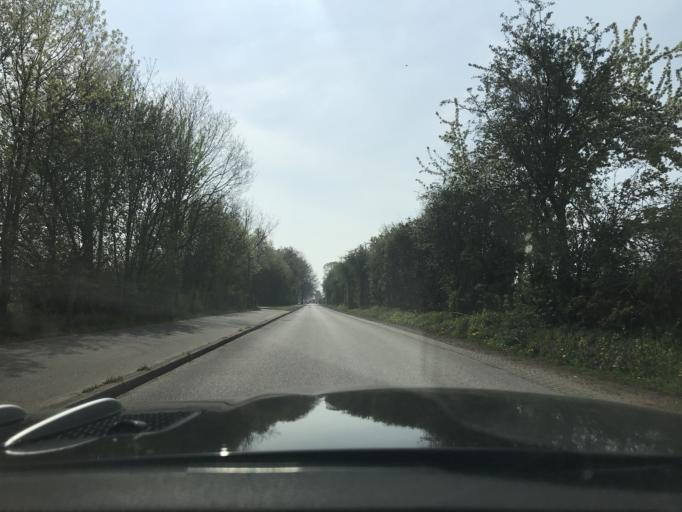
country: DE
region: Schleswig-Holstein
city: Gromitz
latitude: 54.1612
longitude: 10.9861
